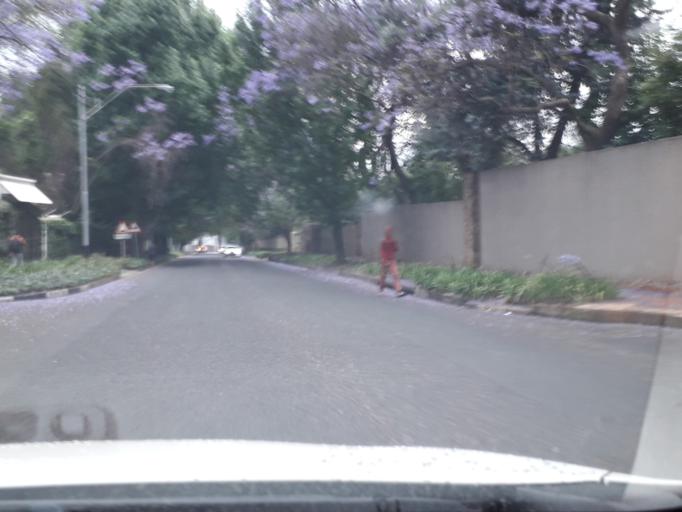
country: ZA
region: Gauteng
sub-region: City of Johannesburg Metropolitan Municipality
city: Johannesburg
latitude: -26.1467
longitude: 28.0471
